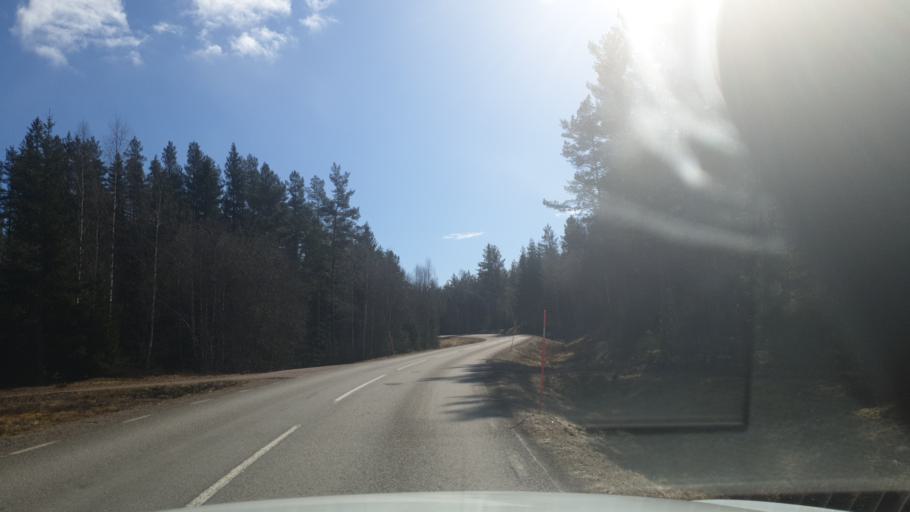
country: SE
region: Vaermland
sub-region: Arjangs Kommun
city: Arjaeng
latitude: 59.5575
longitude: 12.1561
